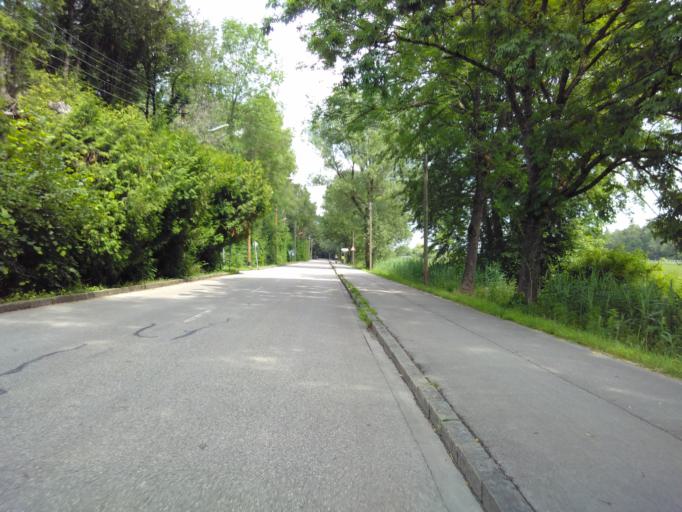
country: DE
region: Bavaria
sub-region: Upper Bavaria
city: Grobenzell
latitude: 48.2064
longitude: 11.3628
